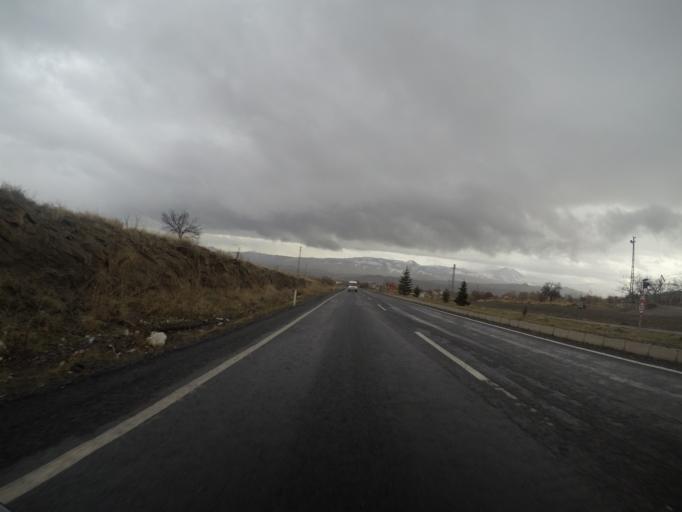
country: TR
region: Kayseri
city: Incesu
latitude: 38.6820
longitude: 35.2005
